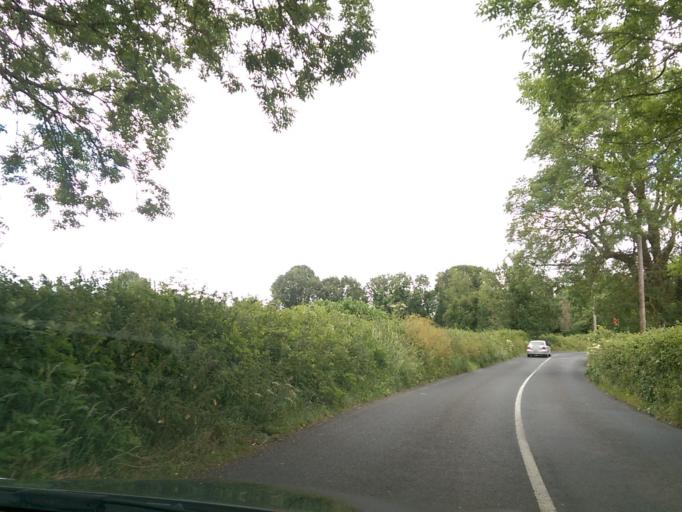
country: IE
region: Munster
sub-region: North Tipperary
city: Nenagh
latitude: 52.8272
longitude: -8.1980
